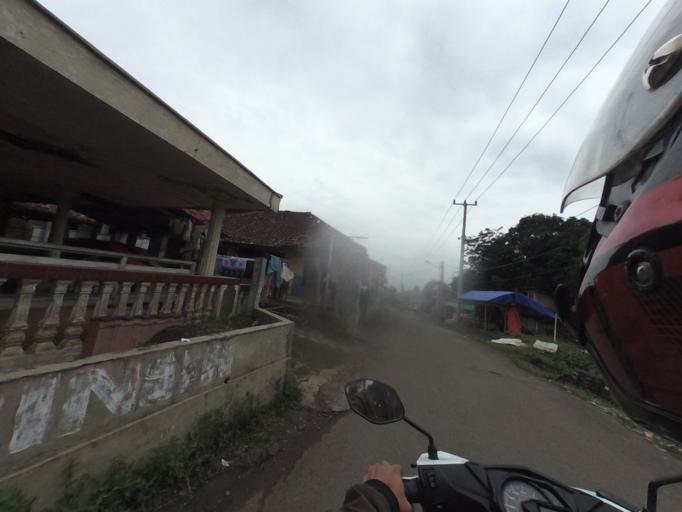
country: ID
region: West Java
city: Bogor
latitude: -6.6193
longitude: 106.7466
